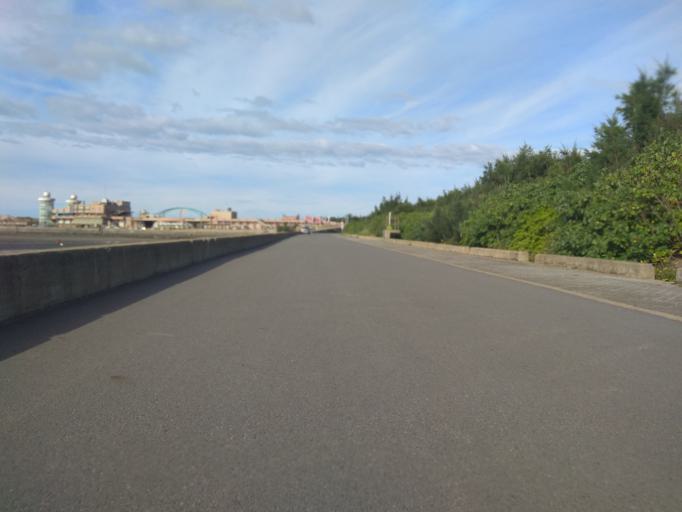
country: TW
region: Taiwan
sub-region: Hsinchu
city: Zhubei
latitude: 24.9845
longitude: 121.0162
